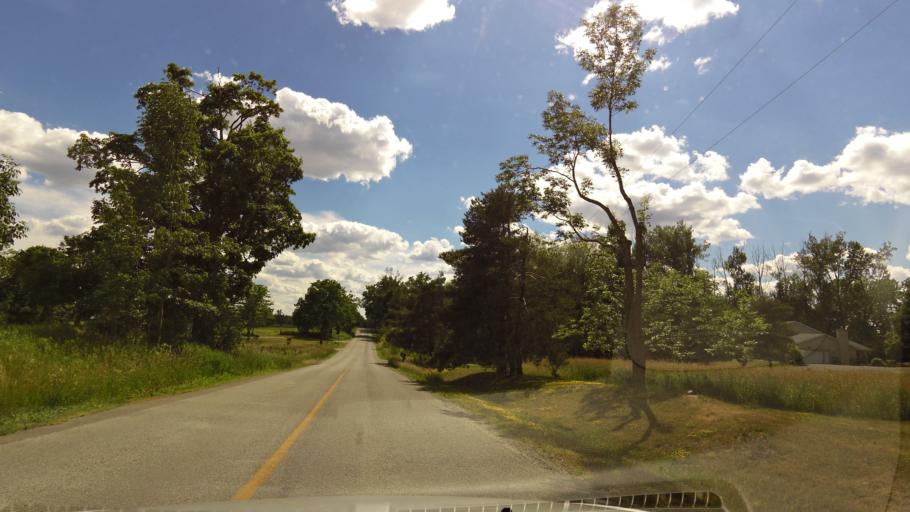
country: CA
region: Ontario
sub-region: Halton
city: Milton
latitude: 43.5764
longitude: -79.9298
